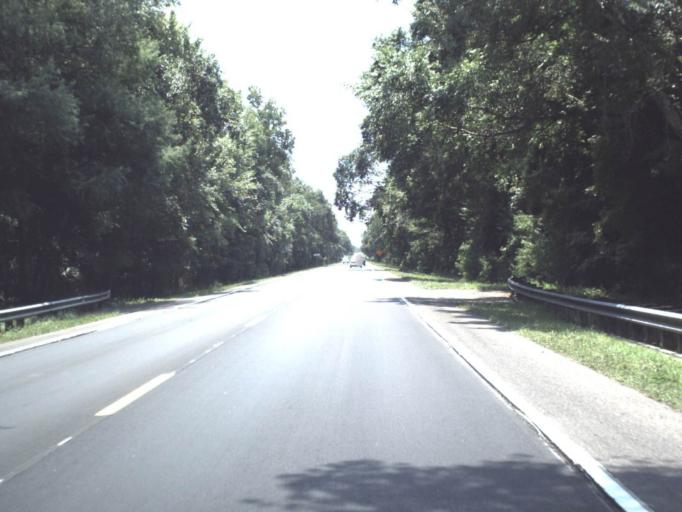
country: US
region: Florida
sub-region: Putnam County
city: Palatka
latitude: 29.4903
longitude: -81.7436
